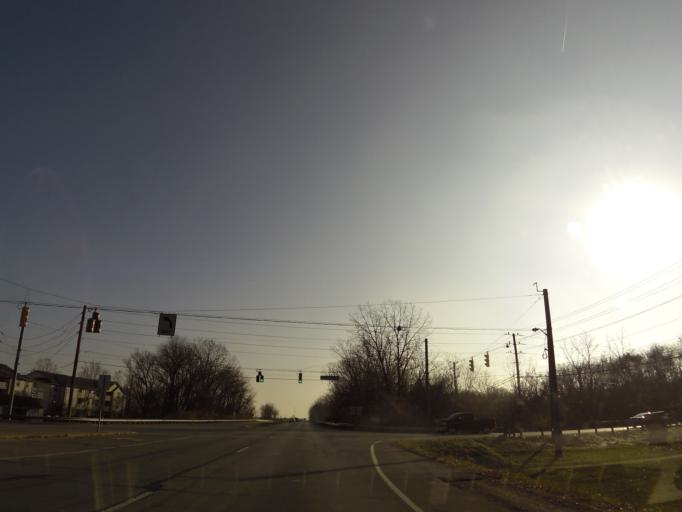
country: US
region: Indiana
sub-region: Marion County
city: Speedway
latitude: 39.8047
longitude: -86.2897
